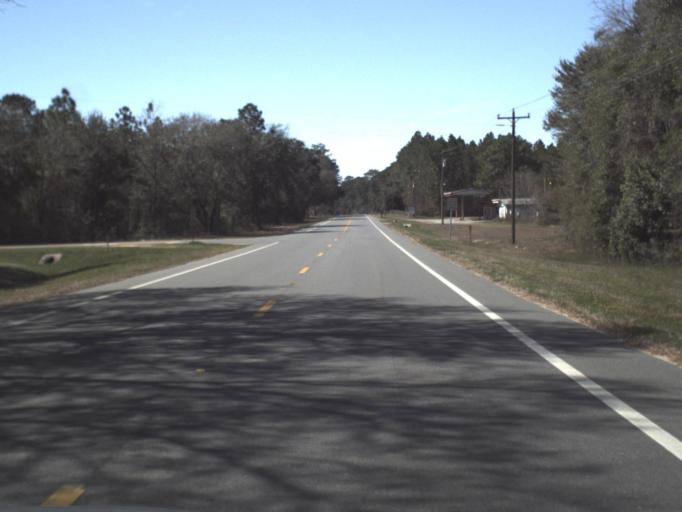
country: US
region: Florida
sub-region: Gadsden County
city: Chattahoochee
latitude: 30.6986
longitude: -84.7694
